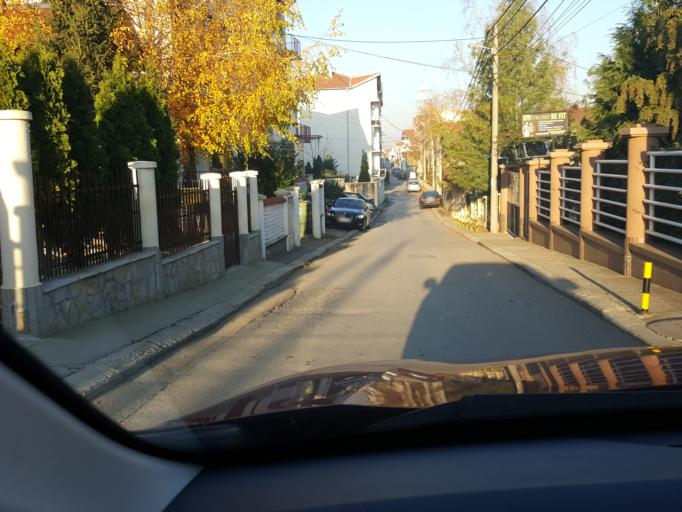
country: RS
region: Central Serbia
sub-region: Belgrade
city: Zvezdara
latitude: 44.7698
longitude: 20.5103
